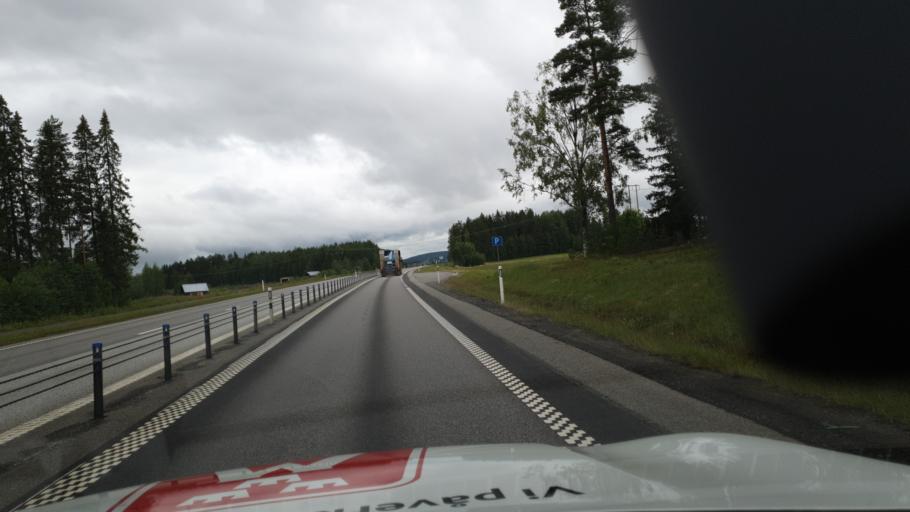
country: SE
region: Vaesterbotten
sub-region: Skelleftea Kommun
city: Skelleftea
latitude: 64.7207
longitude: 20.9849
